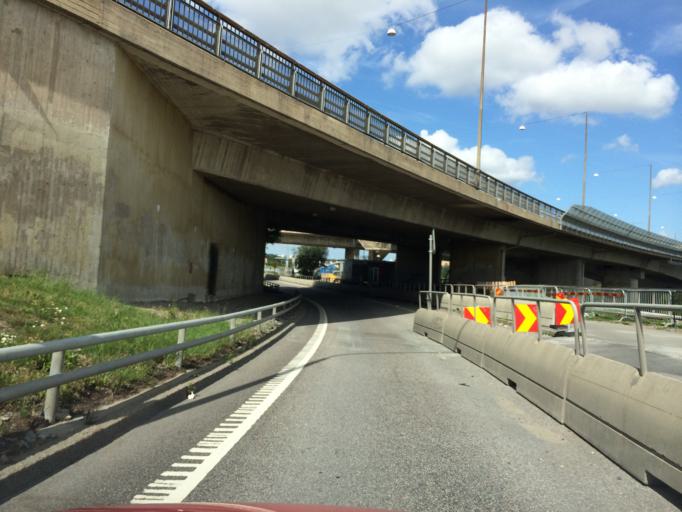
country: SE
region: Stockholm
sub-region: Solna Kommun
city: Solna
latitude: 59.3218
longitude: 17.9973
